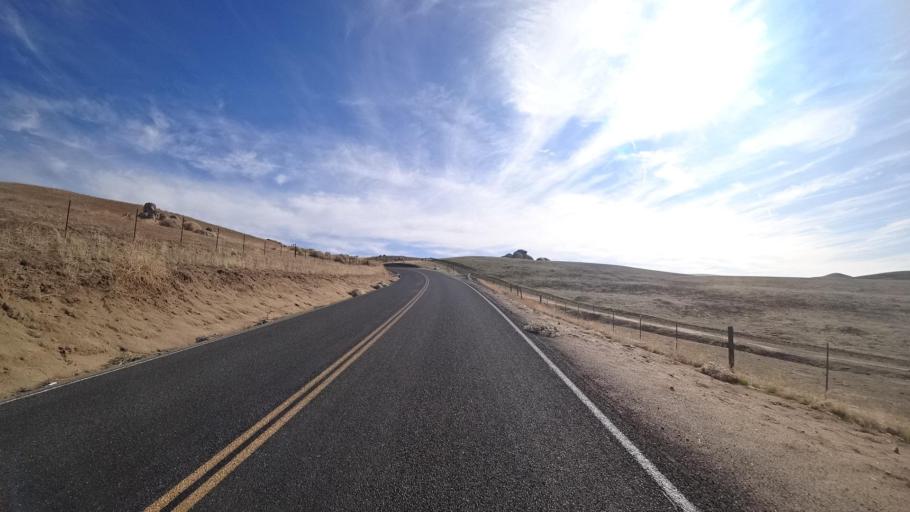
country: US
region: California
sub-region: Kern County
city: Oildale
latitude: 35.6123
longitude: -118.8669
